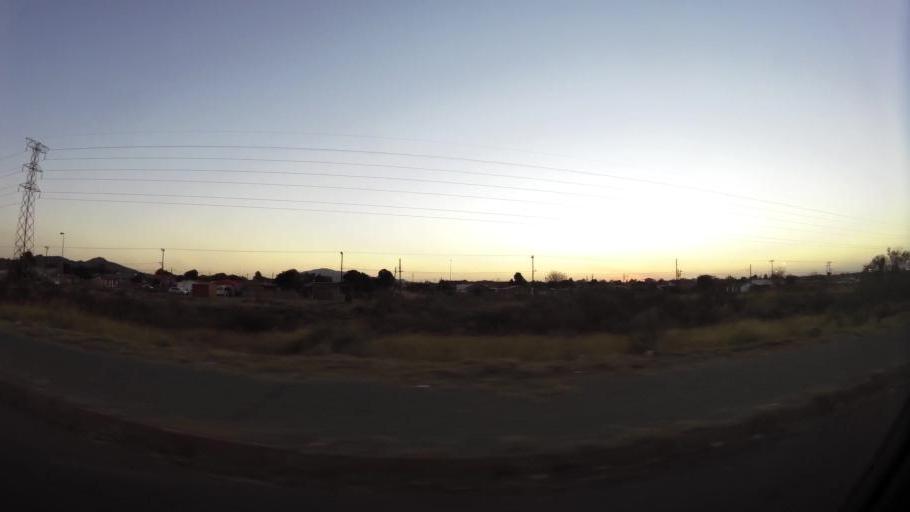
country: ZA
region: North-West
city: Ga-Rankuwa
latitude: -25.5942
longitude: 27.9895
